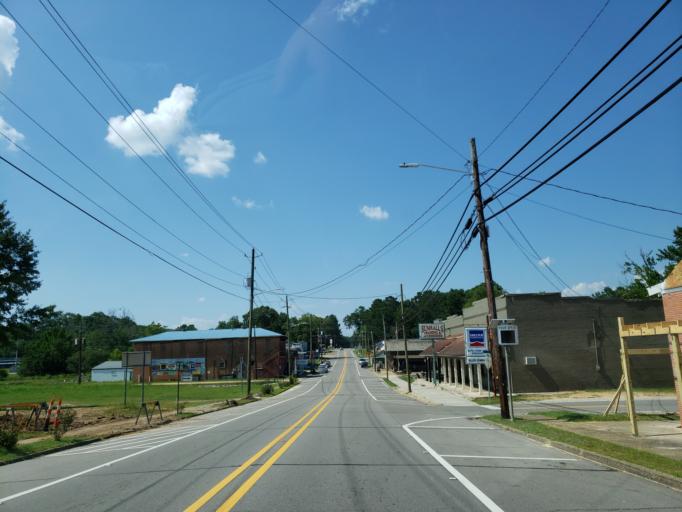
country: US
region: Mississippi
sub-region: Lamar County
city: Sumrall
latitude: 31.4157
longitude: -89.5458
